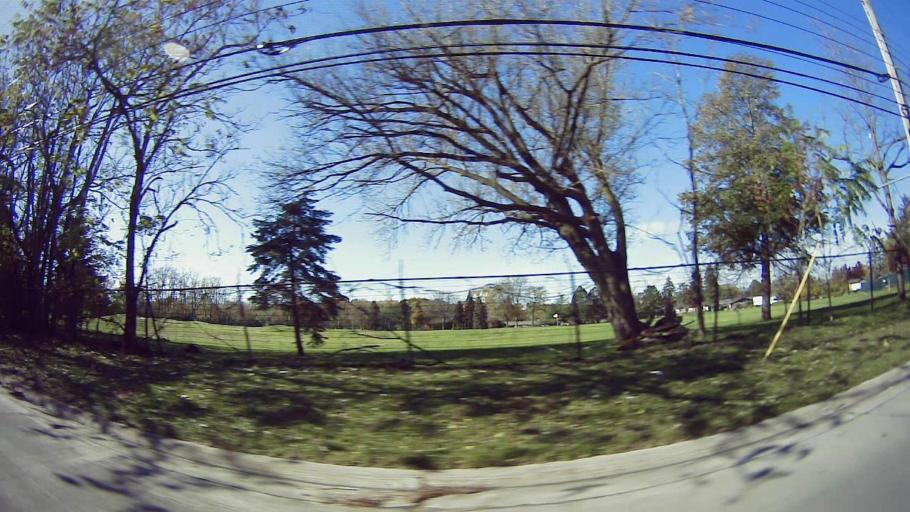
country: US
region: Michigan
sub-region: Oakland County
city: Southfield
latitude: 42.4505
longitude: -83.2598
